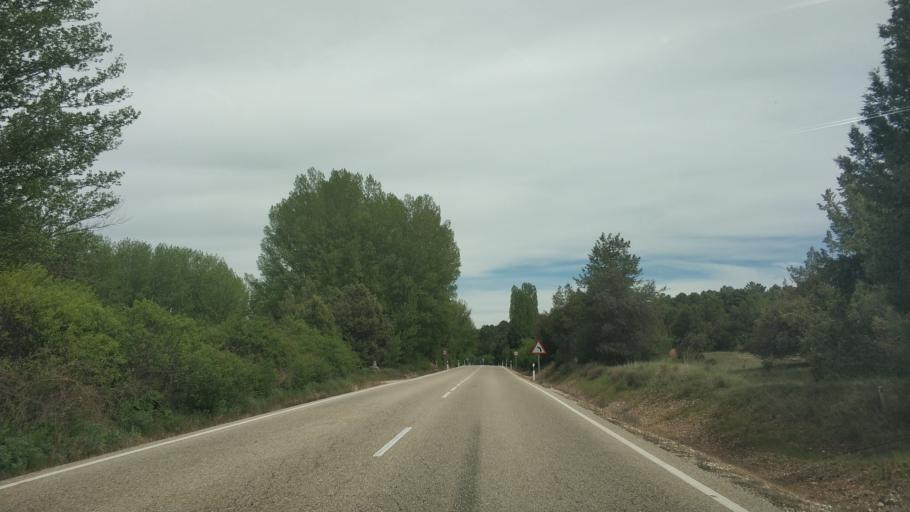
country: ES
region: Castille and Leon
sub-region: Provincia de Soria
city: Valdenebro
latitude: 41.5655
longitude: -2.9966
